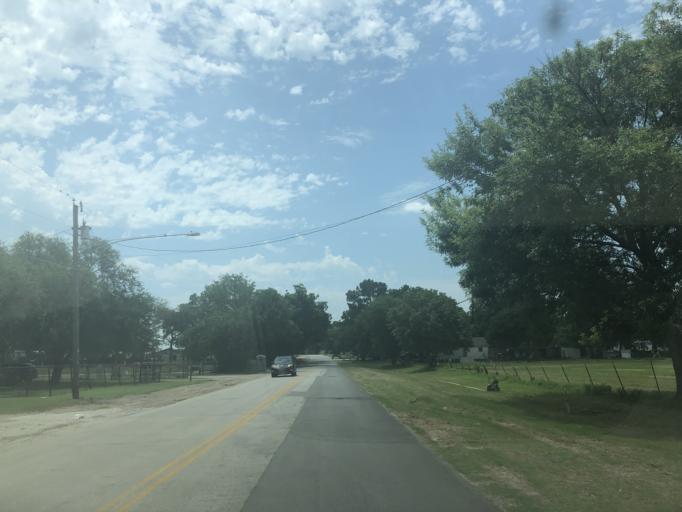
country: US
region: Texas
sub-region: Dallas County
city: Irving
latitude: 32.7915
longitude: -96.9346
